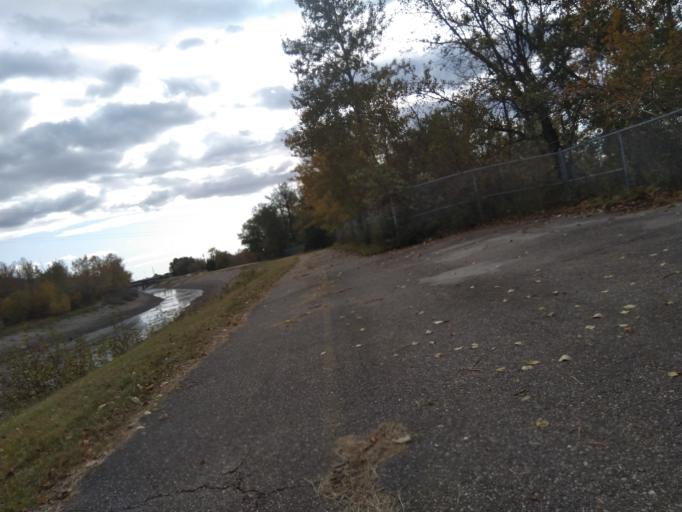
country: CA
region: Alberta
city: Calgary
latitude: 51.0183
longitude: -114.0085
